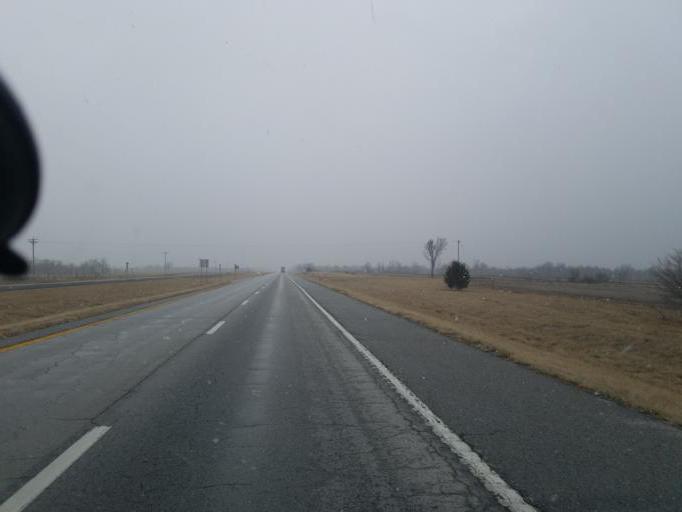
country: US
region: Missouri
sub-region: Macon County
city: La Plata
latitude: 39.9346
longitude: -92.4767
